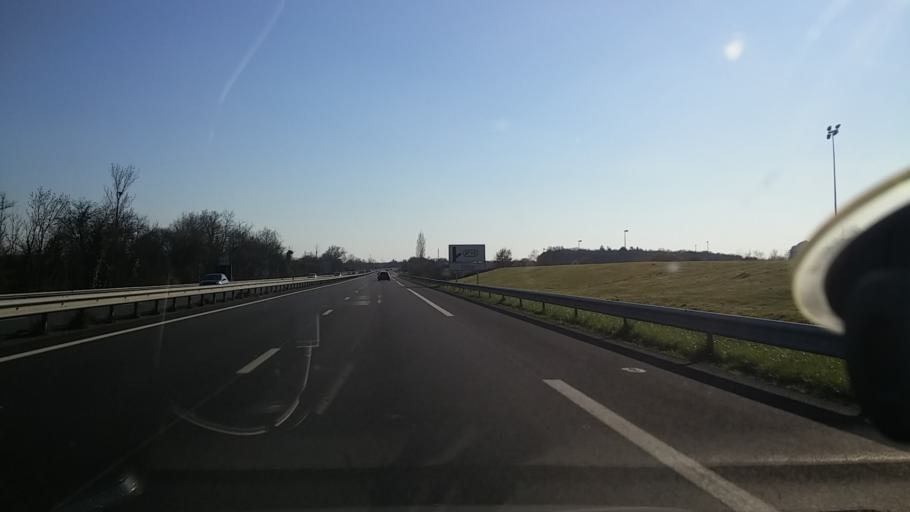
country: FR
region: Centre
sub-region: Departement de l'Indre
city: Luant
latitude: 46.7159
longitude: 1.5962
